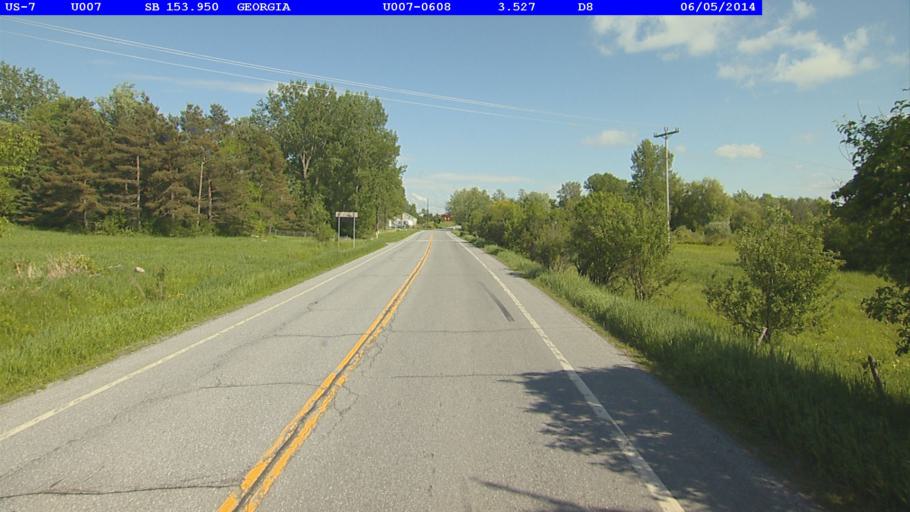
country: US
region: Vermont
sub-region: Chittenden County
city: Milton
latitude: 44.7224
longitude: -73.1173
